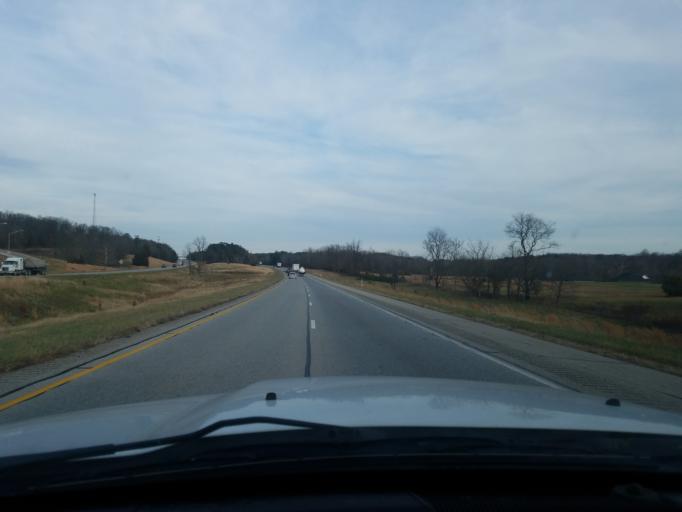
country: US
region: Indiana
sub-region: Floyd County
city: Georgetown
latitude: 38.2721
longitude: -85.9695
